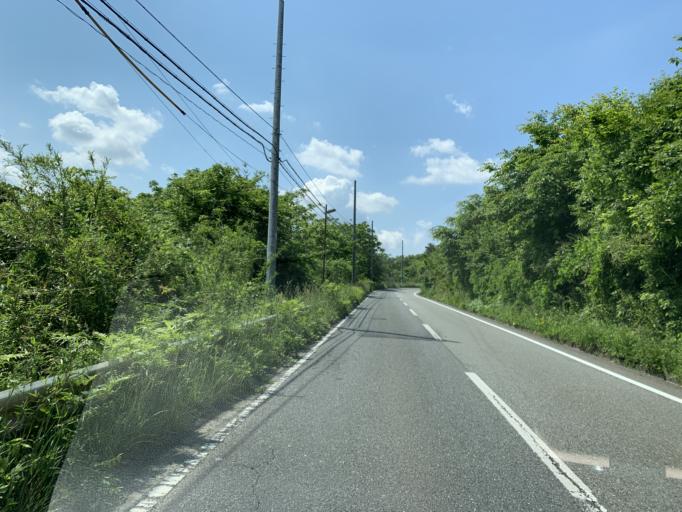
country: JP
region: Miyagi
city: Furukawa
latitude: 38.7198
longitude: 140.9486
